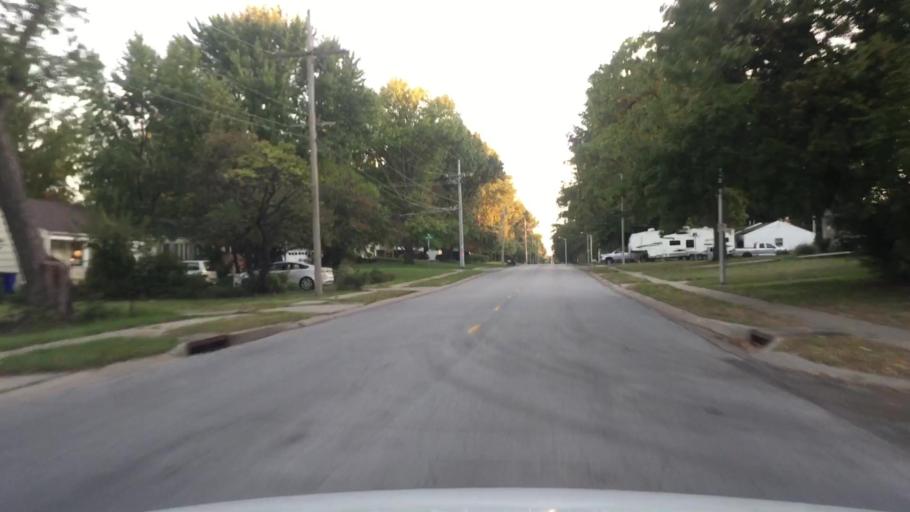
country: US
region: Kansas
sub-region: Johnson County
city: Mission
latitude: 39.0139
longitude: -94.6723
